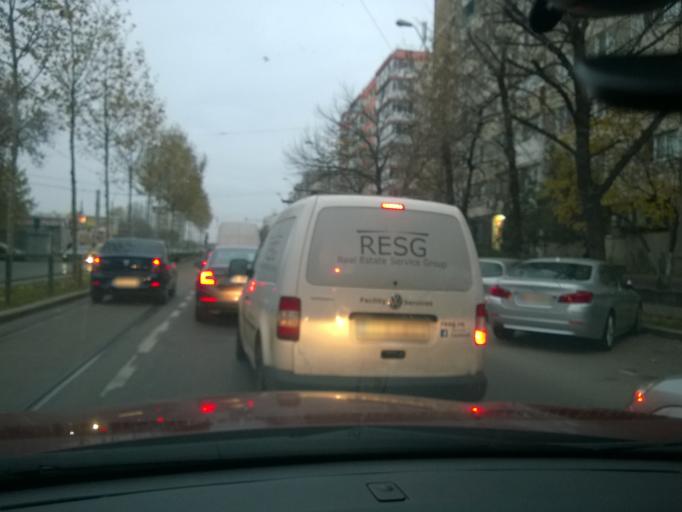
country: RO
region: Ilfov
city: Dobroesti
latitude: 44.4226
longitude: 26.1762
